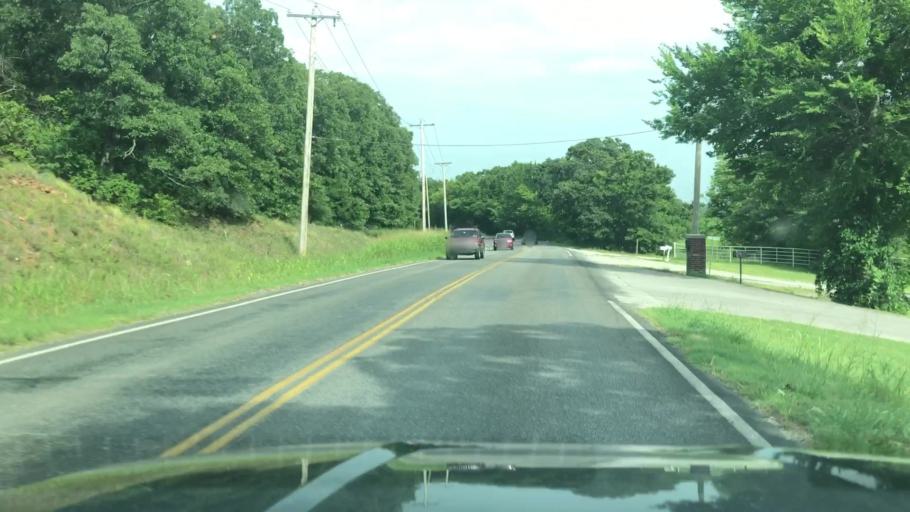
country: US
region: Oklahoma
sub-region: Tulsa County
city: Oakhurst
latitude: 36.0903
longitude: -96.0787
